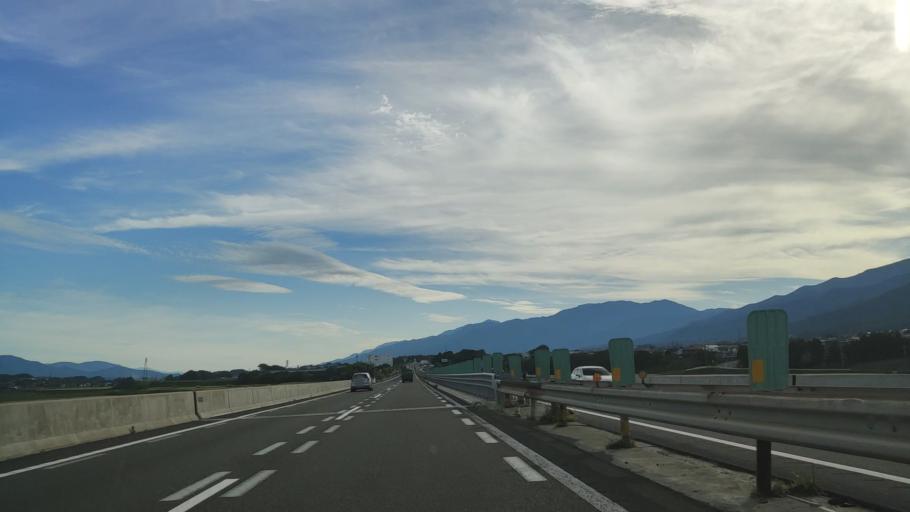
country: JP
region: Nagano
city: Tatsuno
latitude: 35.9569
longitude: 137.9921
